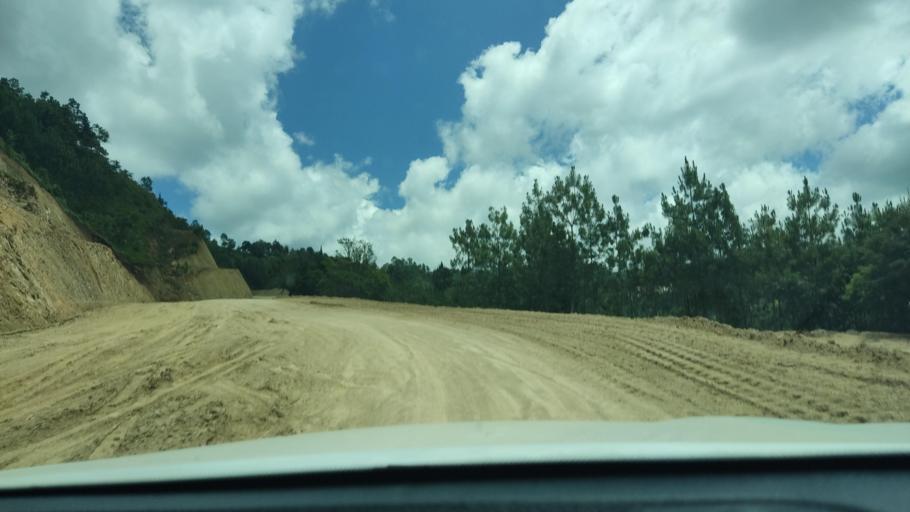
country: GT
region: Chimaltenango
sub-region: Municipio de San Juan Comalapa
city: Comalapa
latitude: 14.7844
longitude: -90.8667
